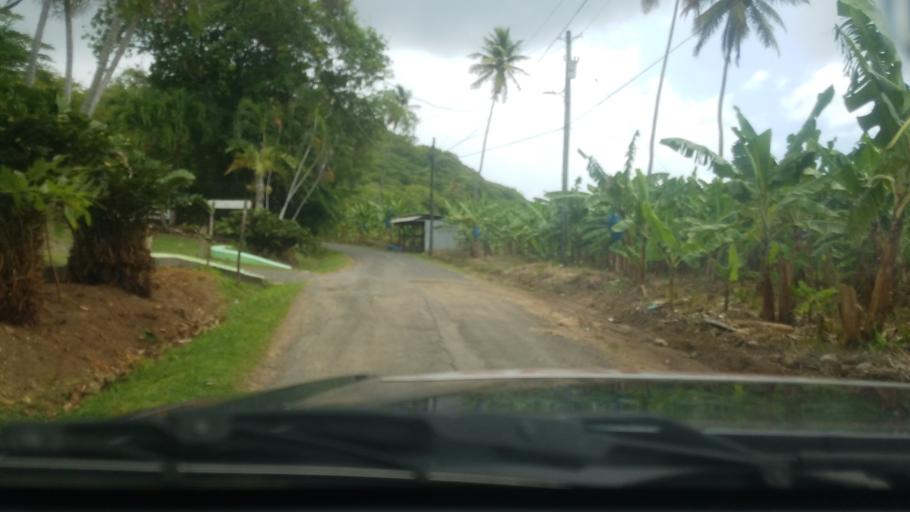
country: LC
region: Praslin
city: Praslin
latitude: 13.8682
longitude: -60.9010
